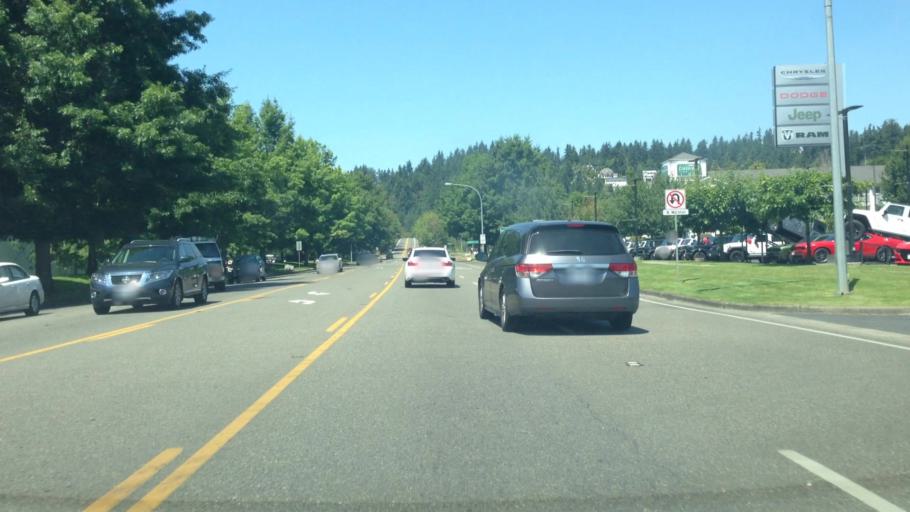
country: US
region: Washington
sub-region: Pierce County
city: North Puyallup
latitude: 47.2078
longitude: -122.2938
